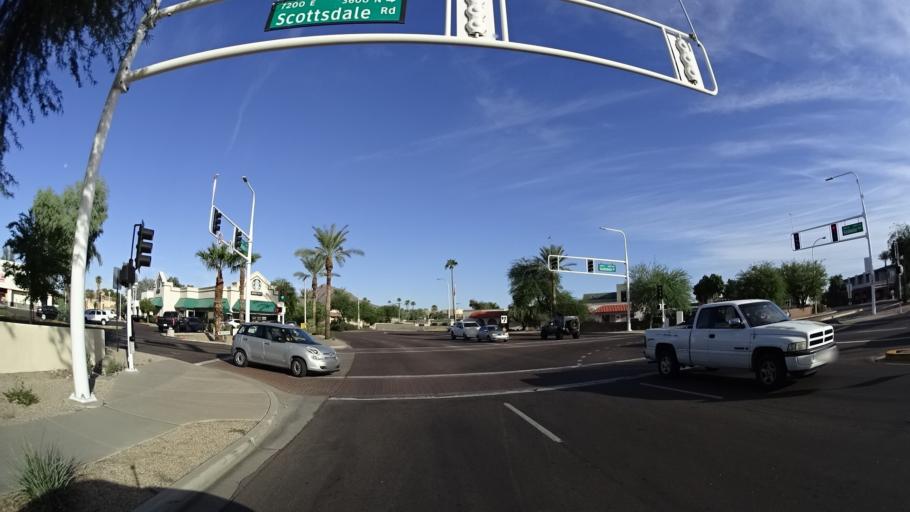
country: US
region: Arizona
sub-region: Maricopa County
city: Scottsdale
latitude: 33.4890
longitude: -111.9267
